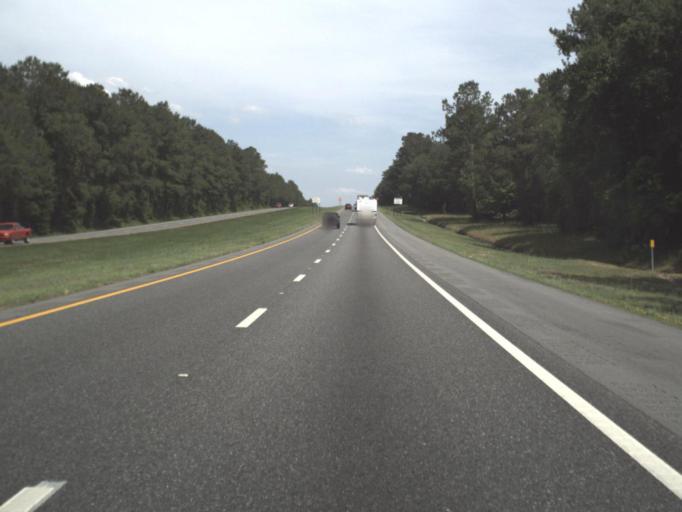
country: US
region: Florida
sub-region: Columbia County
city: Five Points
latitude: 30.2498
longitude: -82.7055
